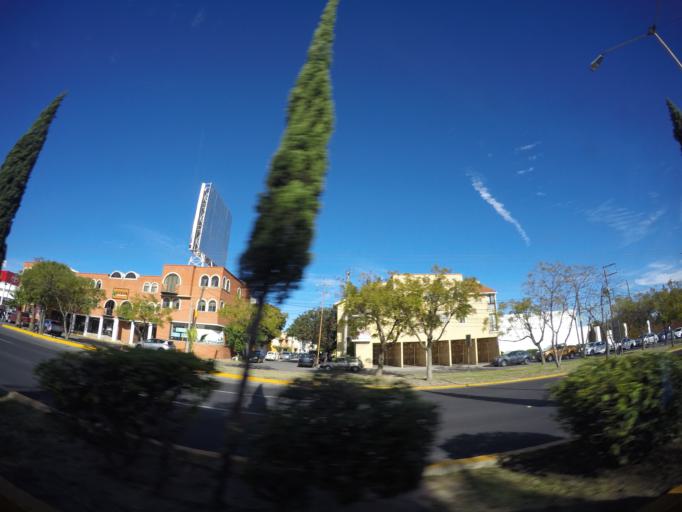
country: MX
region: San Luis Potosi
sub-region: San Luis Potosi
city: San Luis Potosi
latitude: 22.1363
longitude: -101.0269
